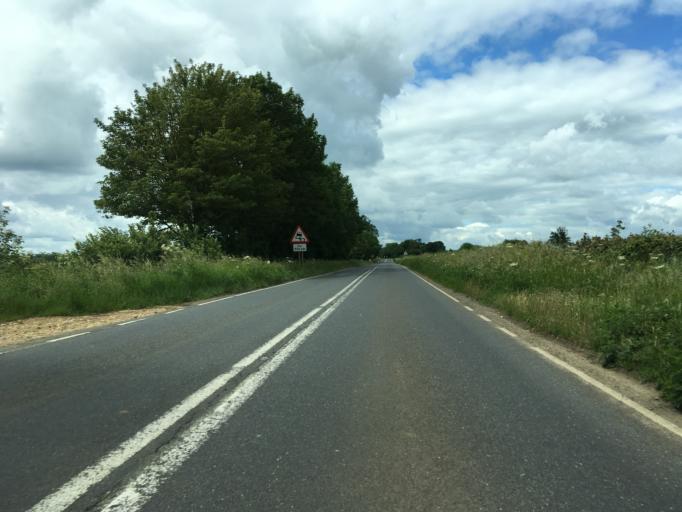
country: GB
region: England
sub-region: Oxfordshire
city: Bloxham
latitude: 52.0040
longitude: -1.3938
